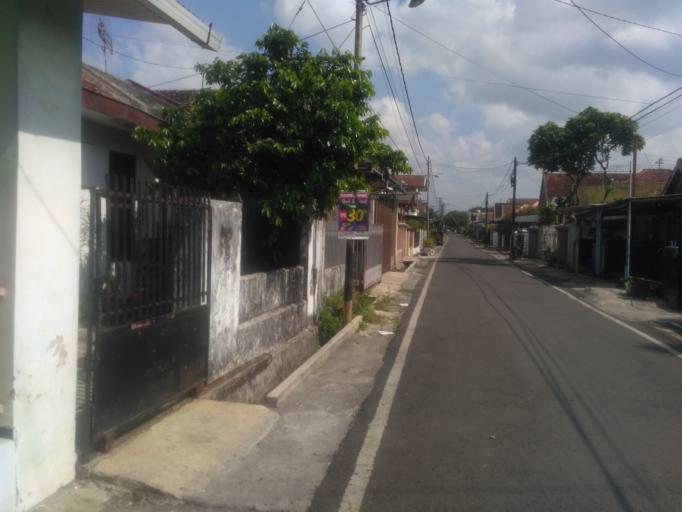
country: ID
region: East Java
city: Malang
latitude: -7.9448
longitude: 112.6387
